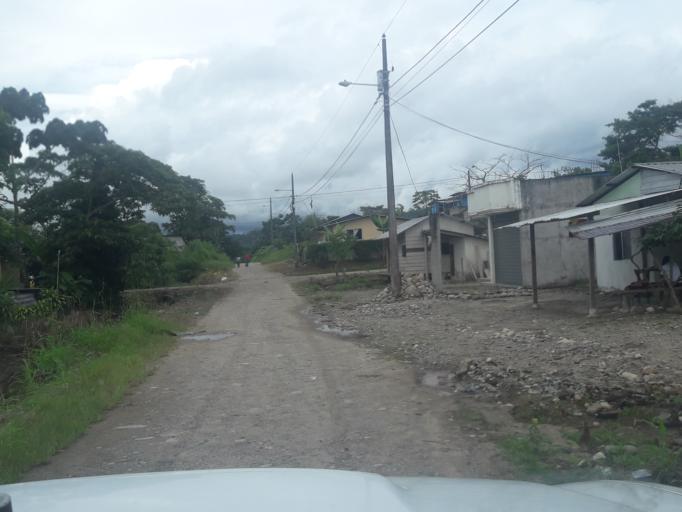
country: EC
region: Napo
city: Archidona
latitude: -0.9477
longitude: -77.8153
